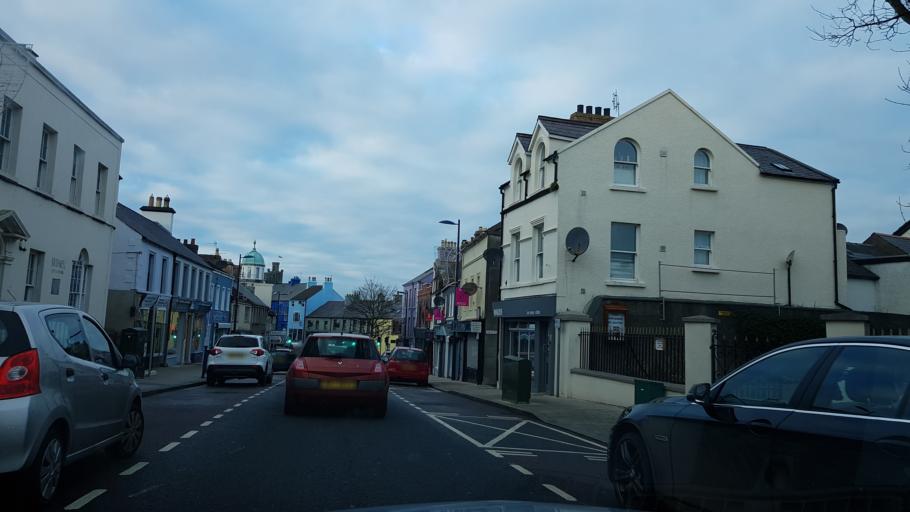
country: GB
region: Northern Ireland
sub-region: Down District
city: Donaghadee
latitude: 54.6419
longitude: -5.5366
